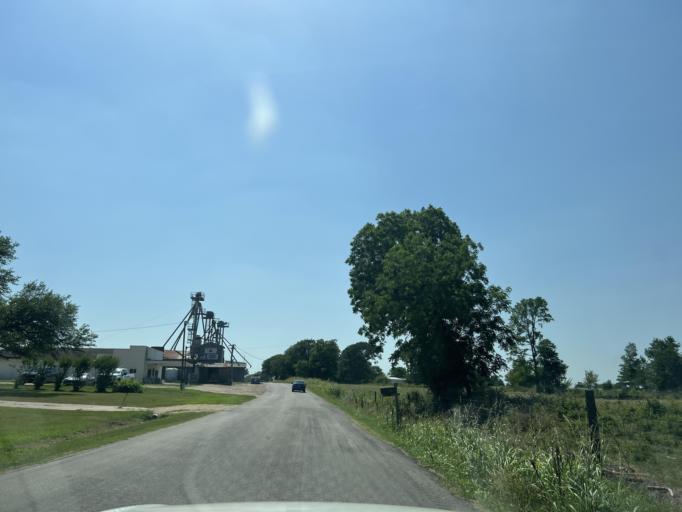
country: US
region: Texas
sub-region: Washington County
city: Brenham
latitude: 30.1562
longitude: -96.4955
